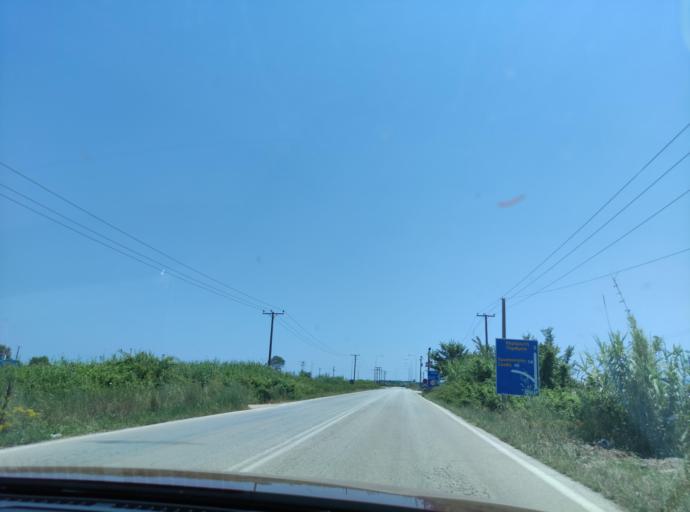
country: GR
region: East Macedonia and Thrace
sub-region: Nomos Kavalas
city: Keramoti
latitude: 40.8706
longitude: 24.7026
